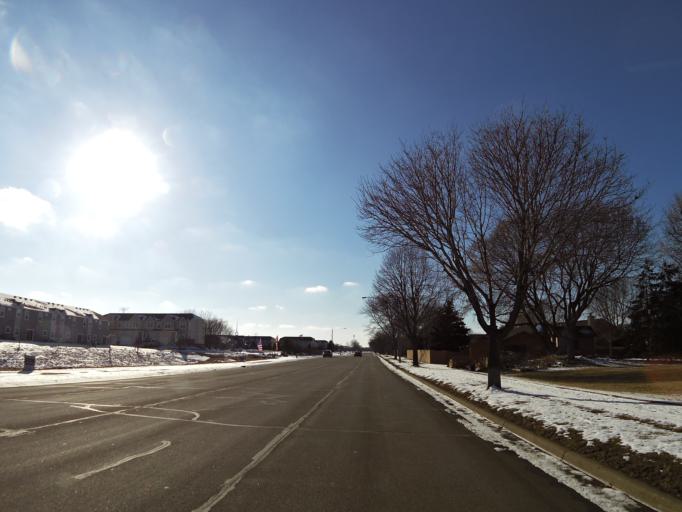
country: US
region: Minnesota
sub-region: Scott County
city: Shakopee
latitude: 44.7815
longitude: -93.4878
